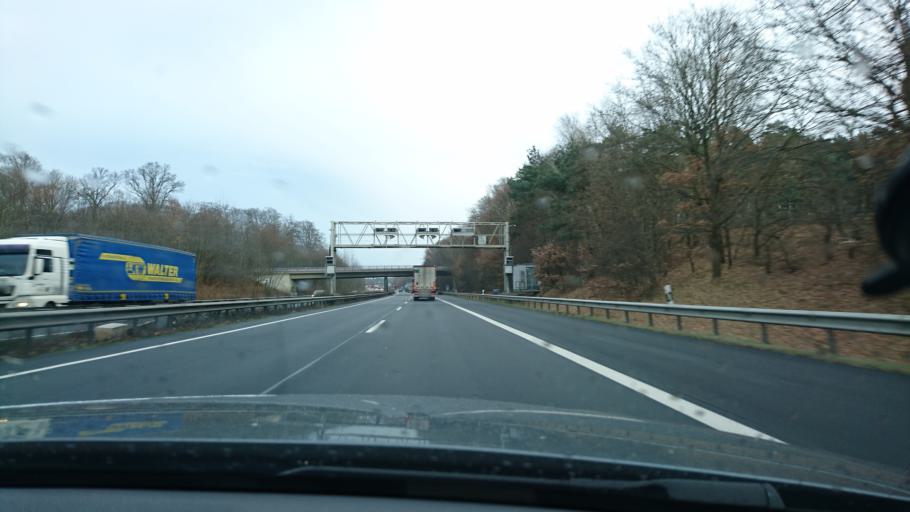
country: DE
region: Lower Saxony
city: Neuenkirchen
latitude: 52.5290
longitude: 8.1105
